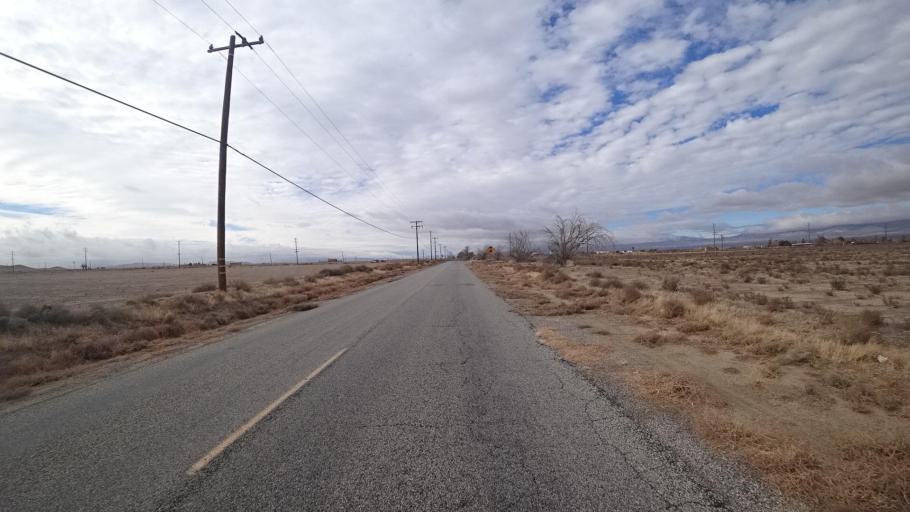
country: US
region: California
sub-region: Kern County
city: Rosamond
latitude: 34.8201
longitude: -118.2881
